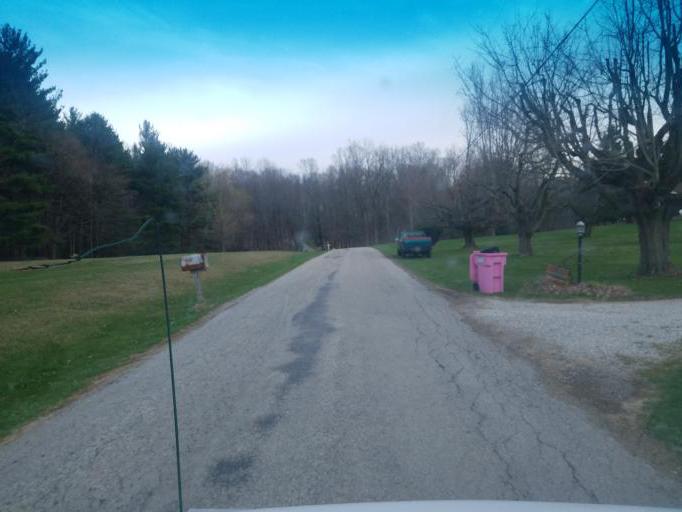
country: US
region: Ohio
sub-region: Richland County
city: Ontario
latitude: 40.7268
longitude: -82.6036
